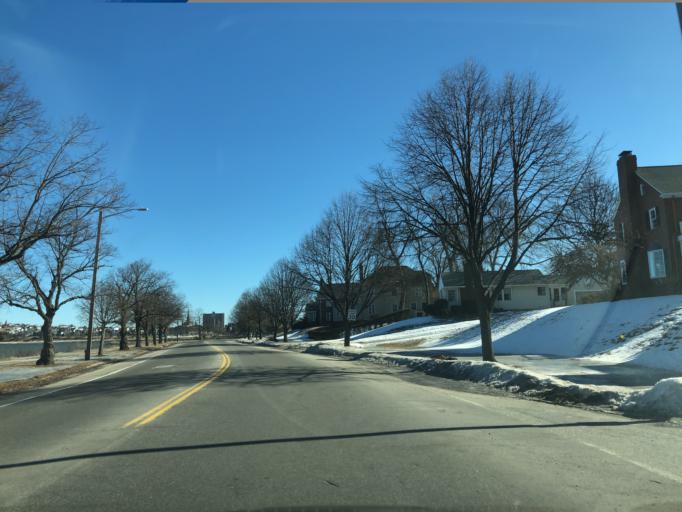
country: US
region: Maine
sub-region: Cumberland County
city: Portland
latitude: 43.6665
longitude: -70.2737
